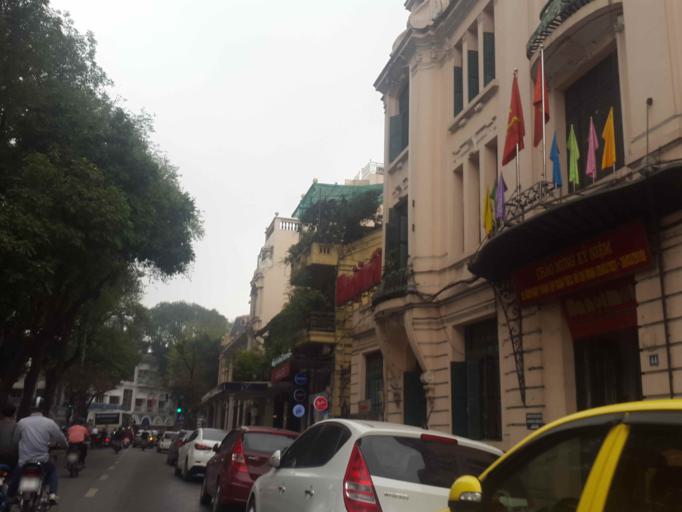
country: VN
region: Ha Noi
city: Hoan Kiem
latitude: 21.0268
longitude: 105.8513
